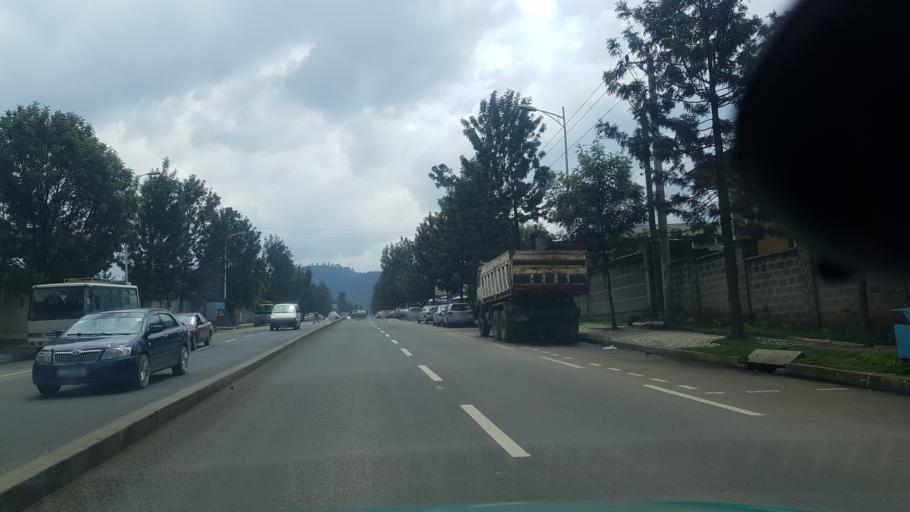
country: ET
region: Adis Abeba
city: Addis Ababa
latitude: 9.0213
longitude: 38.7733
